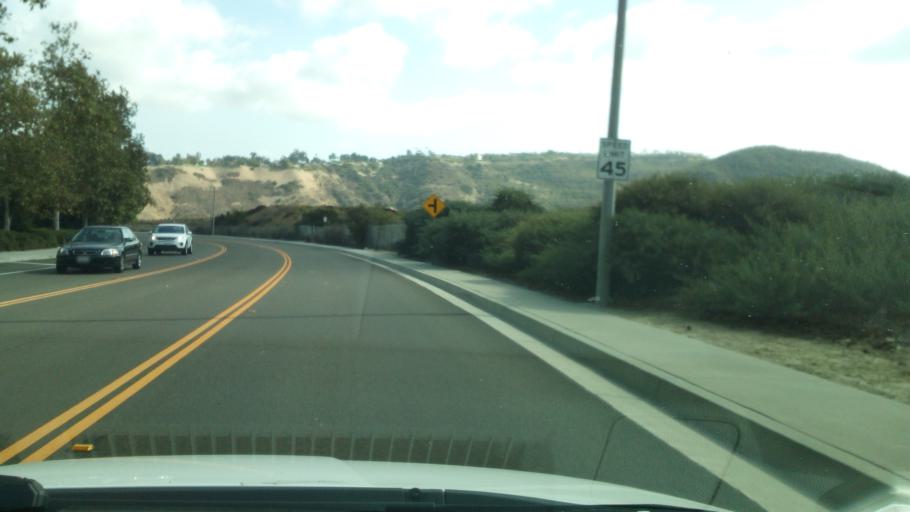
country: US
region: California
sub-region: Orange County
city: Aliso Viejo
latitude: 33.5507
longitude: -117.7294
